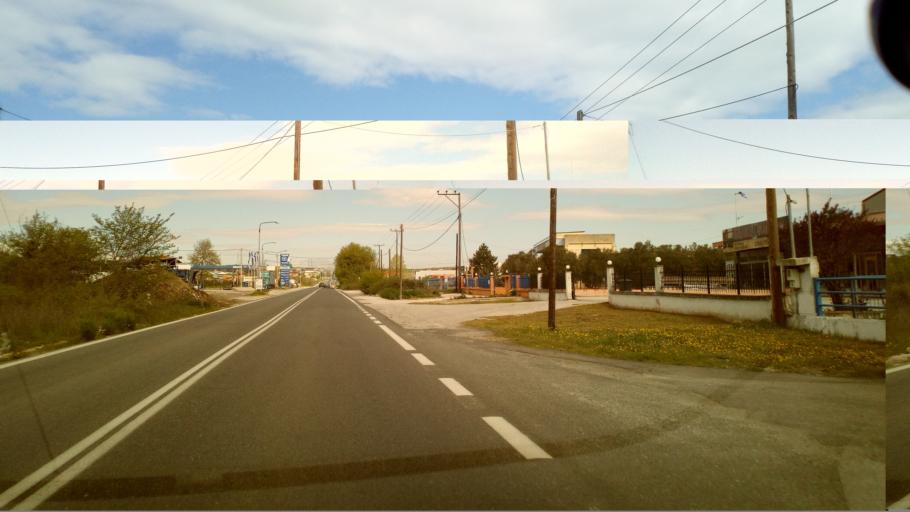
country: GR
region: Central Macedonia
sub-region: Nomos Thessalonikis
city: Drymos
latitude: 40.7698
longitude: 22.9519
